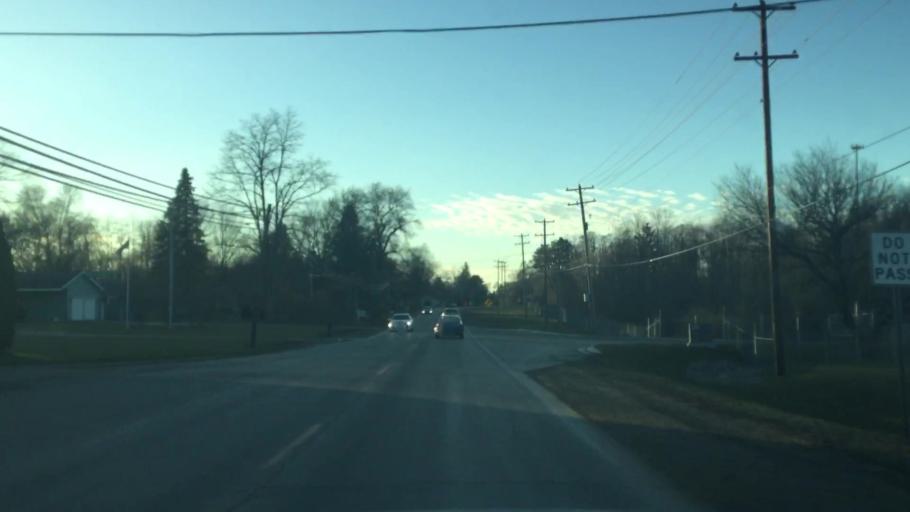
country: US
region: Michigan
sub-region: Genesee County
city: Linden
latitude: 42.8108
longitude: -83.8024
